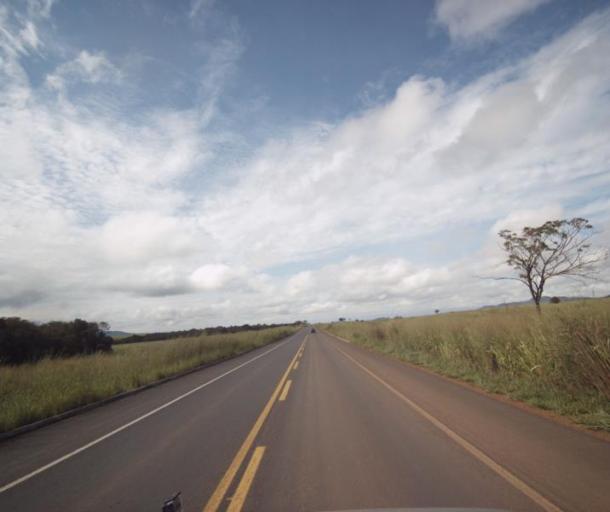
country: BR
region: Goias
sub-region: Padre Bernardo
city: Padre Bernardo
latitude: -15.4462
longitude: -48.6174
